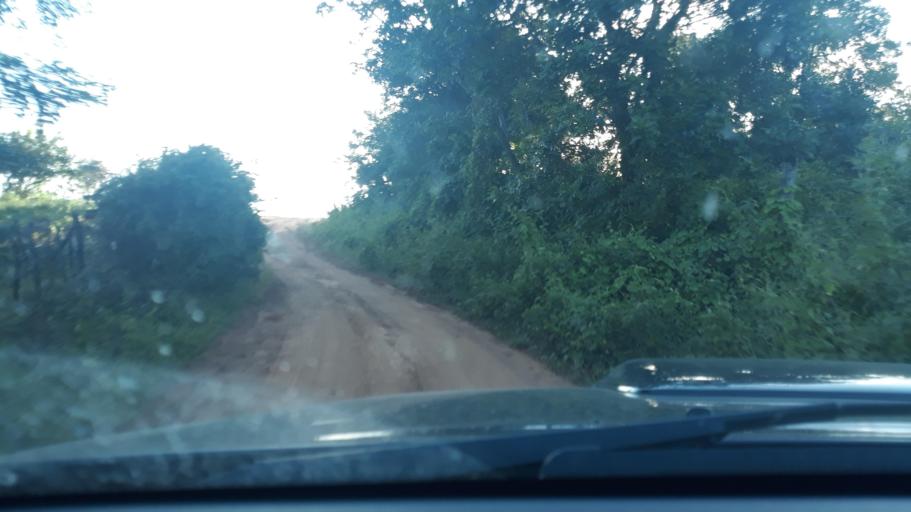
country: BR
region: Bahia
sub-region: Riacho De Santana
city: Riacho de Santana
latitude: -13.8451
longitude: -42.7657
